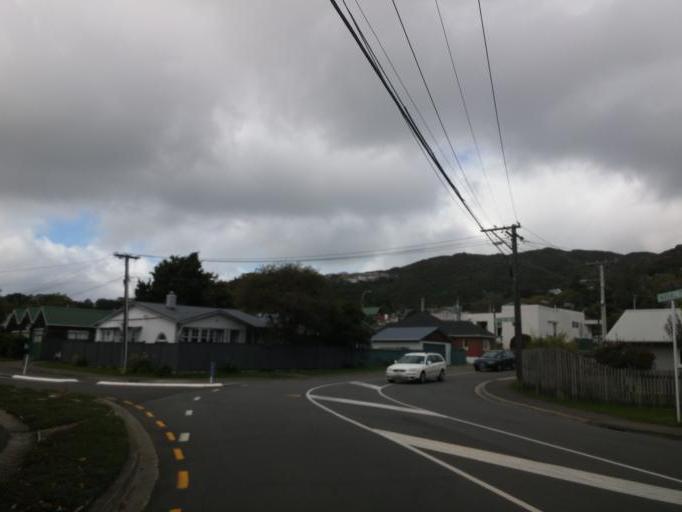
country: NZ
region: Wellington
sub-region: Wellington City
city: Brooklyn
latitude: -41.2859
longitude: 174.7278
